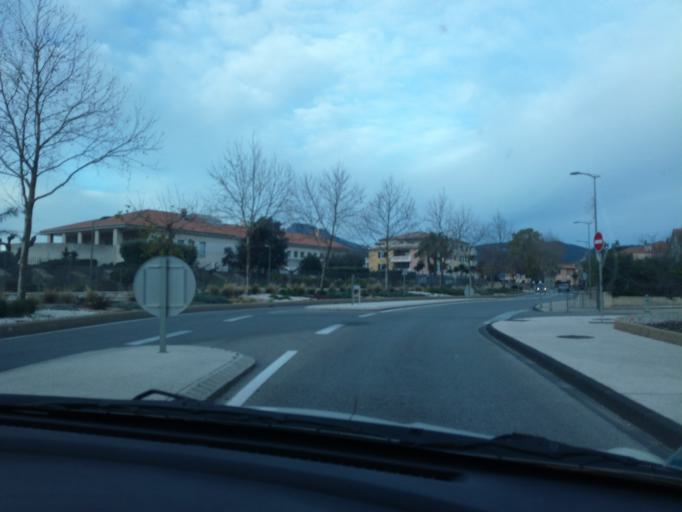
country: FR
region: Provence-Alpes-Cote d'Azur
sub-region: Departement du Var
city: La Crau
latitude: 43.1465
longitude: 6.0777
